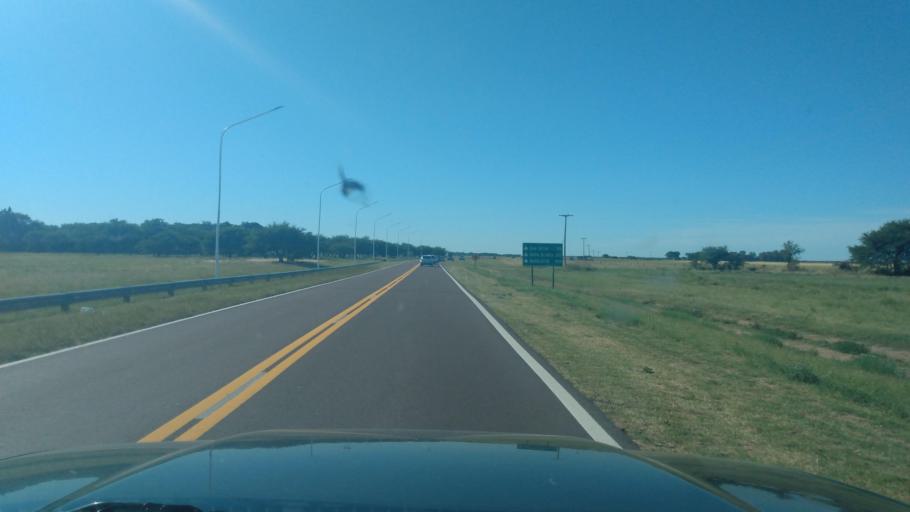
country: AR
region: La Pampa
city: Doblas
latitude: -37.0383
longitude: -64.2871
